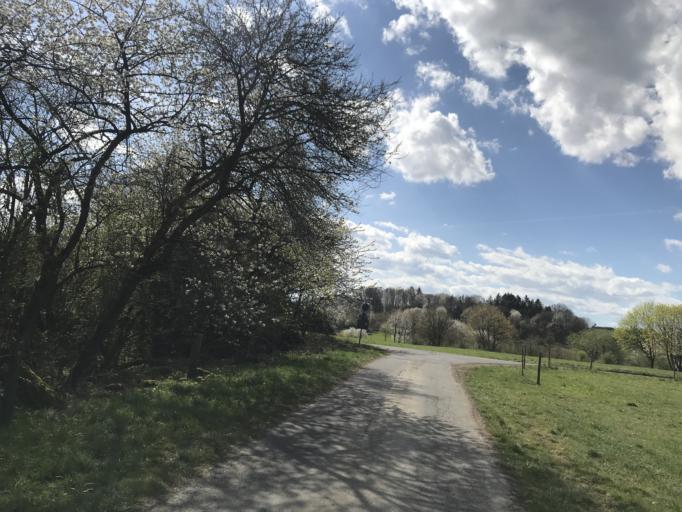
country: DE
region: Hesse
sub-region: Regierungsbezirk Giessen
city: Ebsdorfergrund
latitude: 50.6983
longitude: 8.8298
